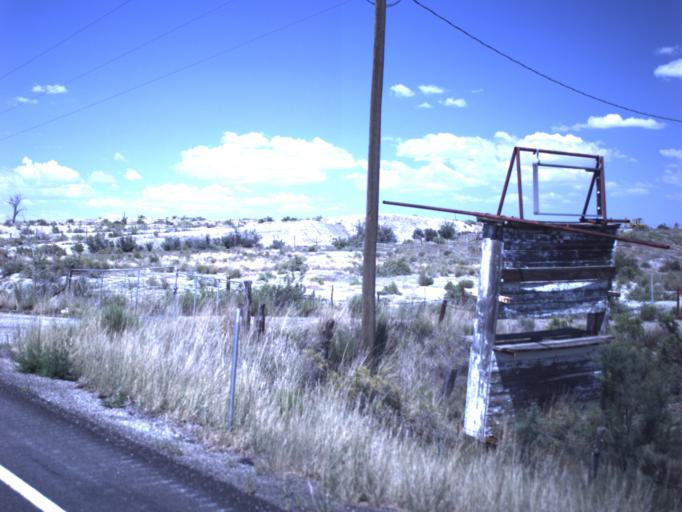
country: US
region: Utah
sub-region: Emery County
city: Huntington
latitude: 39.3148
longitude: -110.9643
